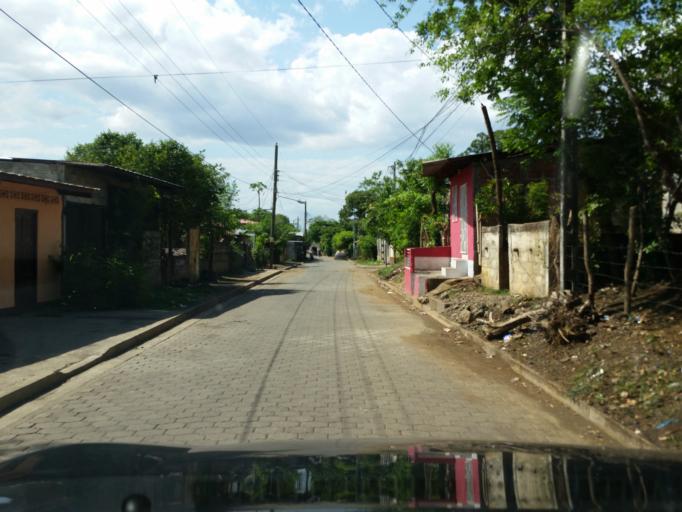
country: NI
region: Leon
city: Leon
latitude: 12.4326
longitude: -86.8988
